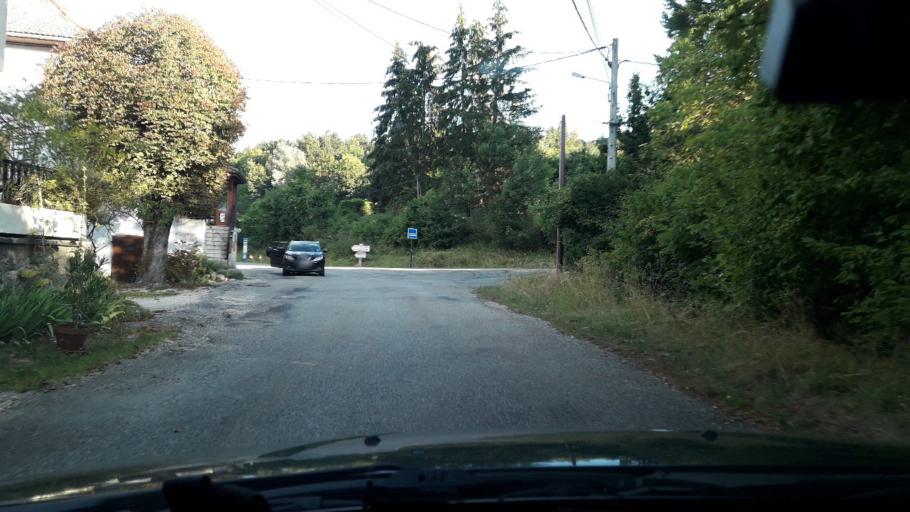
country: FR
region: Rhone-Alpes
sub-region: Departement de l'Isere
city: Mens
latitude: 44.8276
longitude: 5.6070
